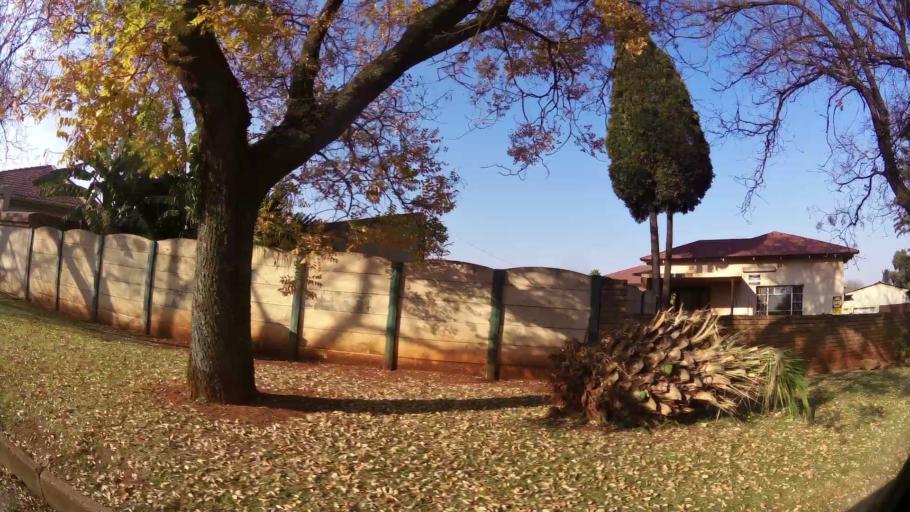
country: ZA
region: Gauteng
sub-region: Ekurhuleni Metropolitan Municipality
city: Brakpan
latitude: -26.2520
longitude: 28.3736
